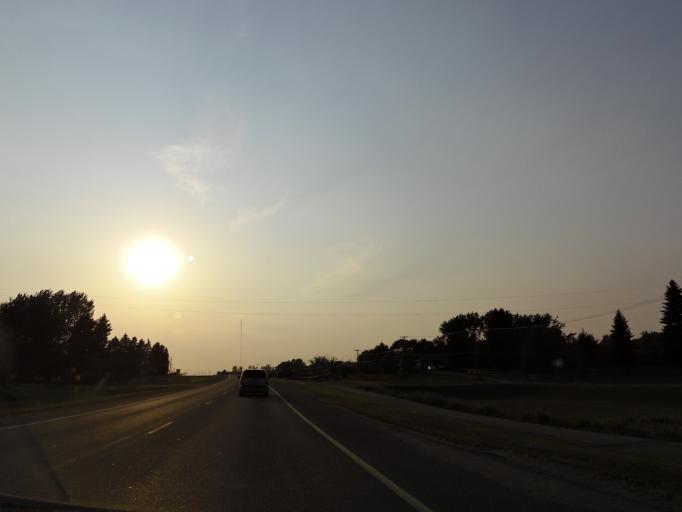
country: US
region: North Dakota
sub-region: Traill County
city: Mayville
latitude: 47.4980
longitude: -97.3390
